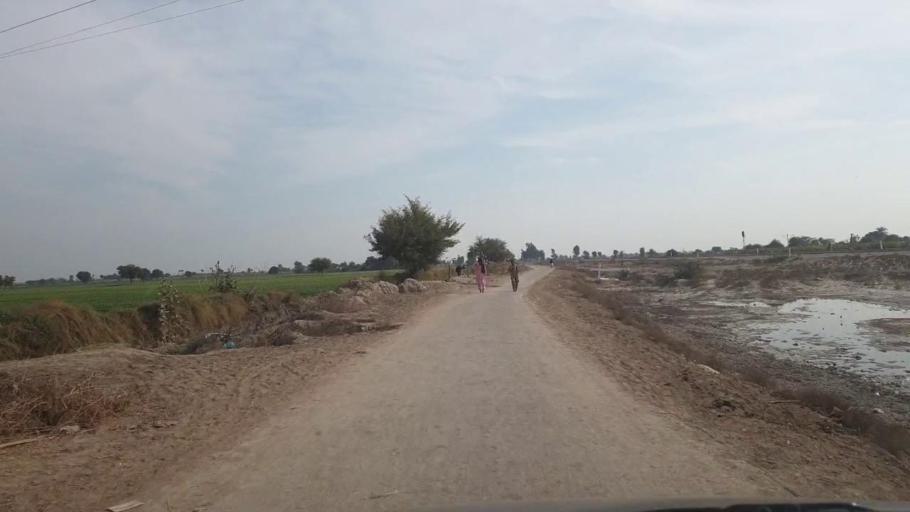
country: PK
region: Sindh
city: Nawabshah
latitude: 26.0923
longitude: 68.4826
